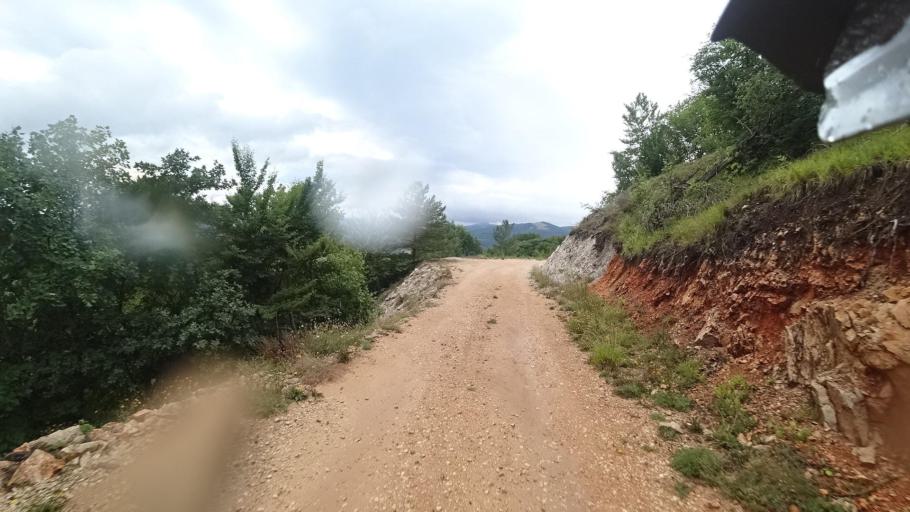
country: HR
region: Licko-Senjska
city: Jezerce
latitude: 44.7219
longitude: 15.6562
